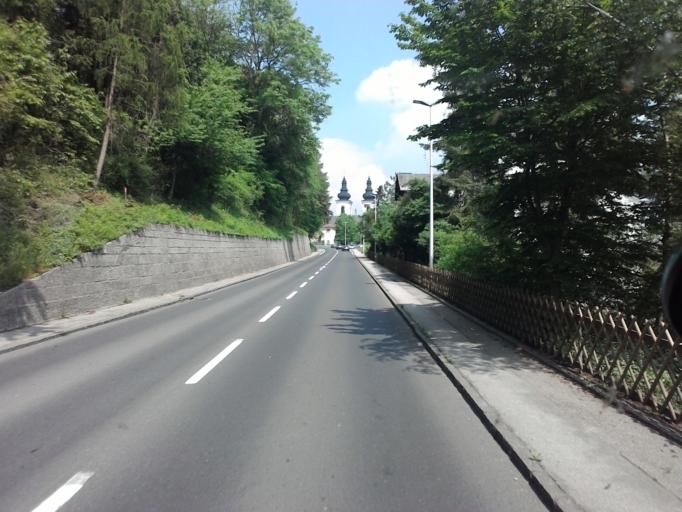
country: AT
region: Upper Austria
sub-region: Politischer Bezirk Kirchdorf an der Krems
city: Kremsmunster
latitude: 48.0528
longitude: 14.1247
